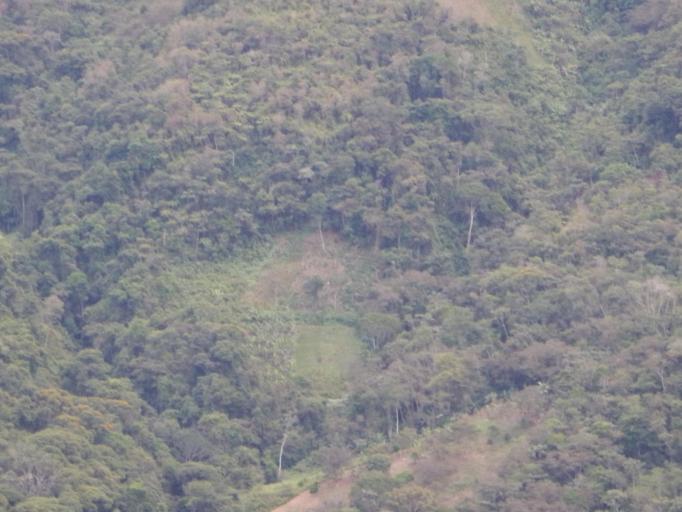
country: BO
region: La Paz
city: Coroico
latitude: -16.1132
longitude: -67.7735
